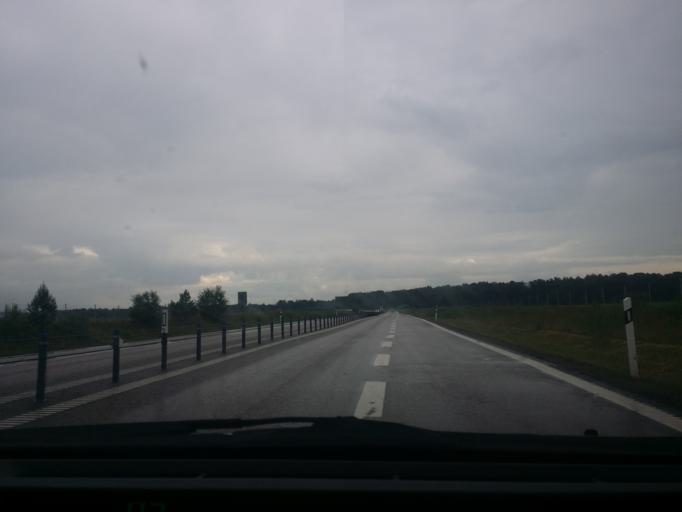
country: SE
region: Vaestmanland
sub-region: Arboga Kommun
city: Arboga
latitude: 59.4265
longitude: 15.8905
